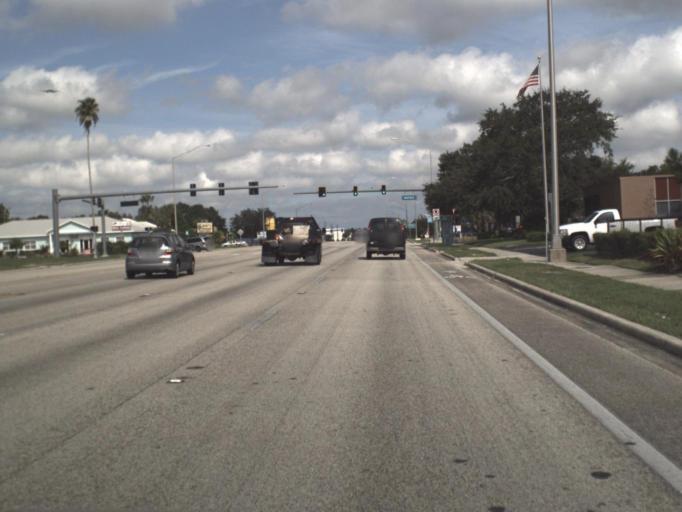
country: US
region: Florida
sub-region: Manatee County
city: Whitfield
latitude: 27.4086
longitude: -82.5700
